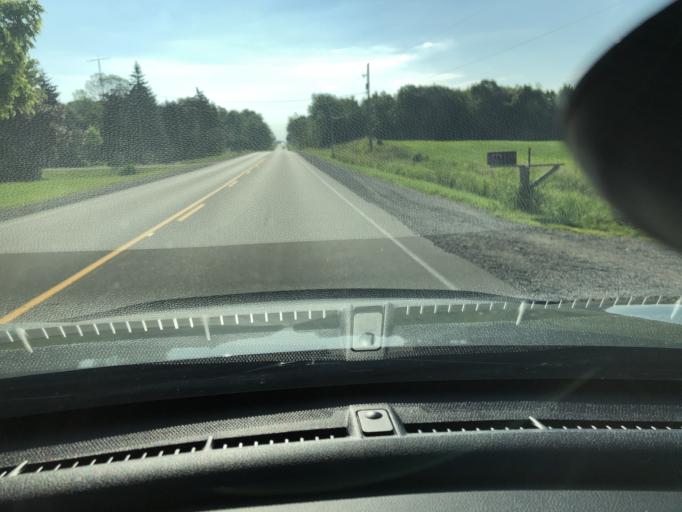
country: CA
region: Ontario
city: Stratford
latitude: 43.4246
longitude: -80.7980
